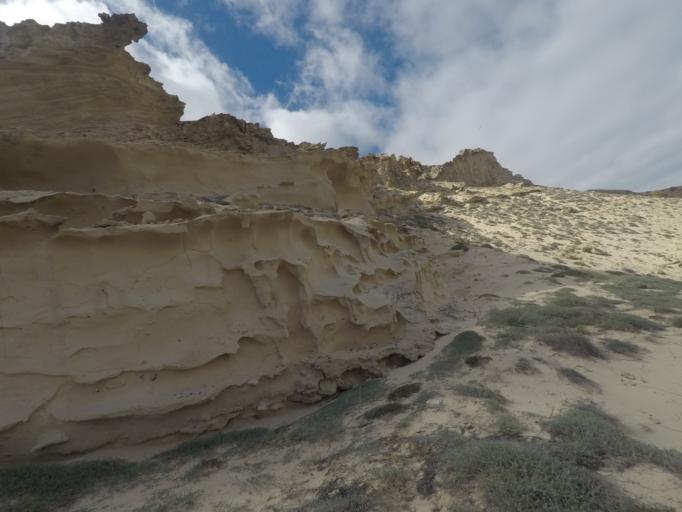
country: PT
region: Madeira
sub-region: Porto Santo
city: Vila de Porto Santo
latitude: 33.0721
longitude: -16.2968
